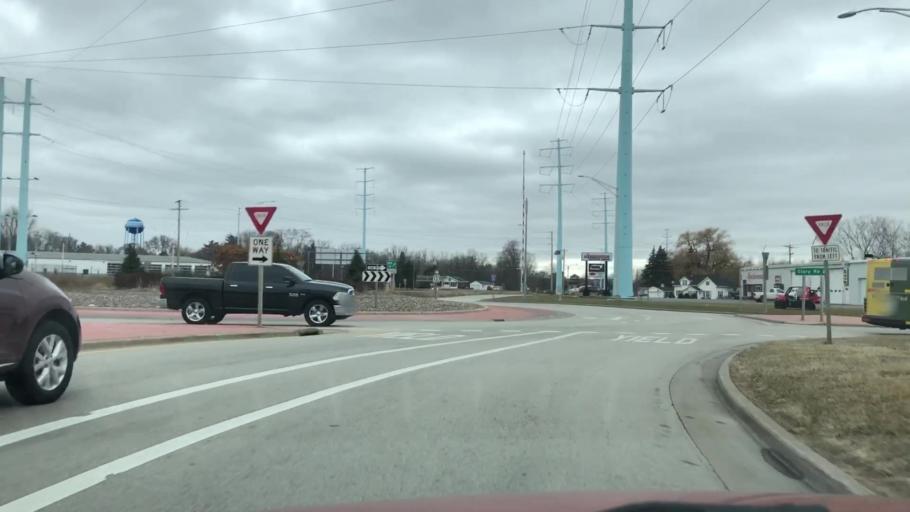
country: US
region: Wisconsin
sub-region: Brown County
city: De Pere
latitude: 44.4571
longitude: -88.0766
